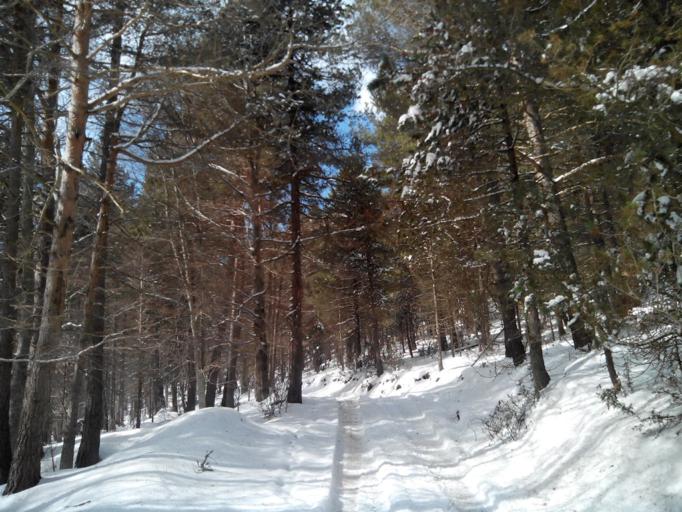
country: ES
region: Catalonia
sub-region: Provincia de Barcelona
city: Sant Julia de Cerdanyola
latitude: 42.2047
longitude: 1.9406
